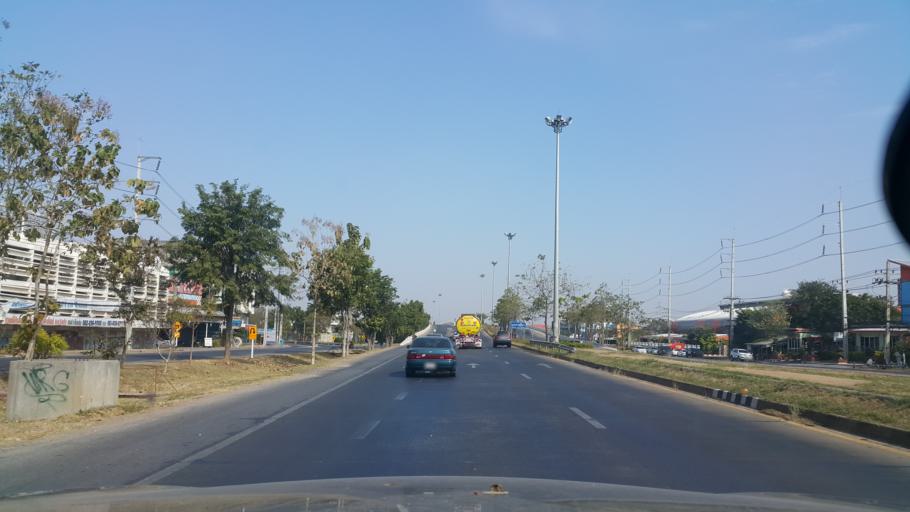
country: TH
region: Nakhon Ratchasima
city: Nakhon Ratchasima
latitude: 14.9558
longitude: 102.0536
